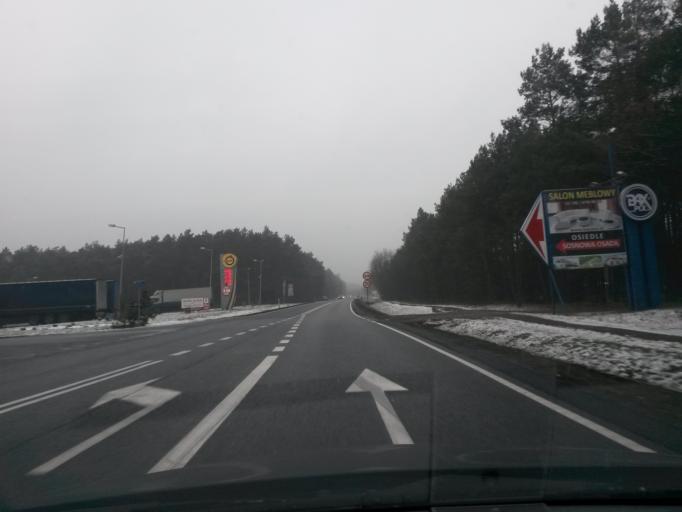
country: PL
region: Kujawsko-Pomorskie
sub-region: Powiat torunski
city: Wielka Nieszawka
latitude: 52.9944
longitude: 18.4683
